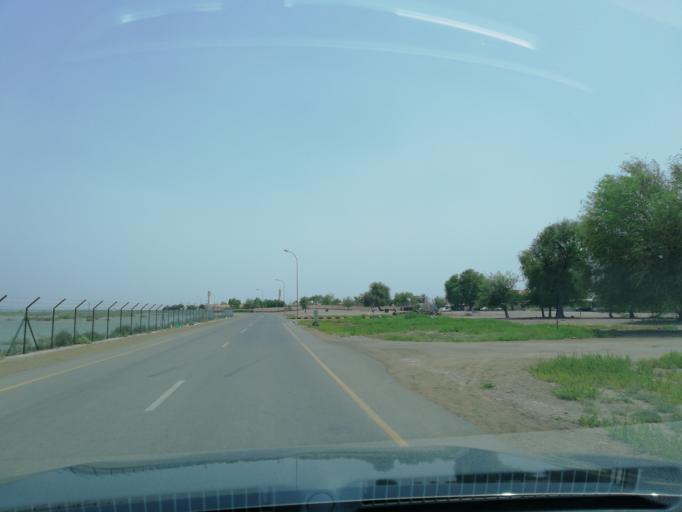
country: OM
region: Al Batinah
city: Shinas
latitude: 24.7494
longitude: 56.4676
